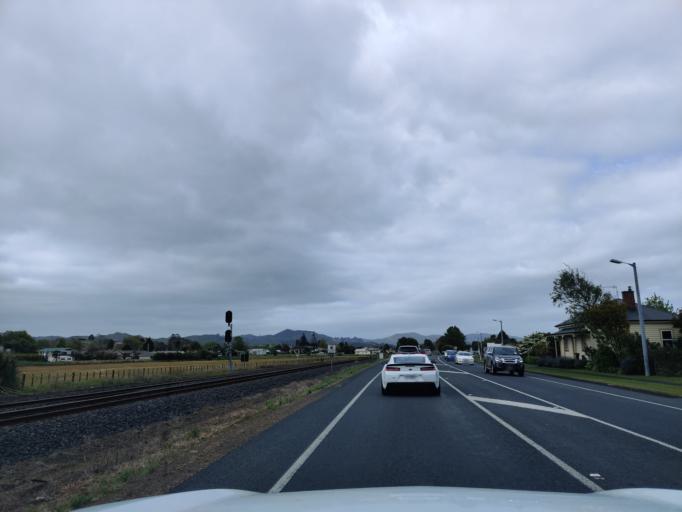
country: NZ
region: Waikato
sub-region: Waikato District
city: Te Kauwhata
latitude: -37.5330
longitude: 175.1593
